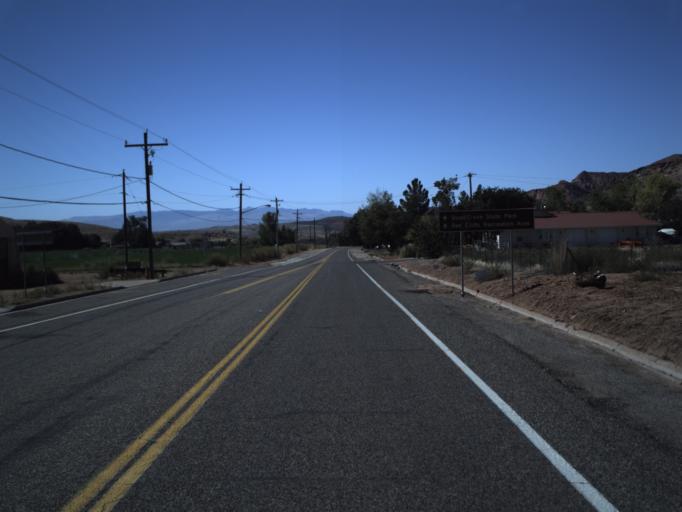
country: US
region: Utah
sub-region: Washington County
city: Toquerville
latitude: 37.2327
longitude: -113.3675
